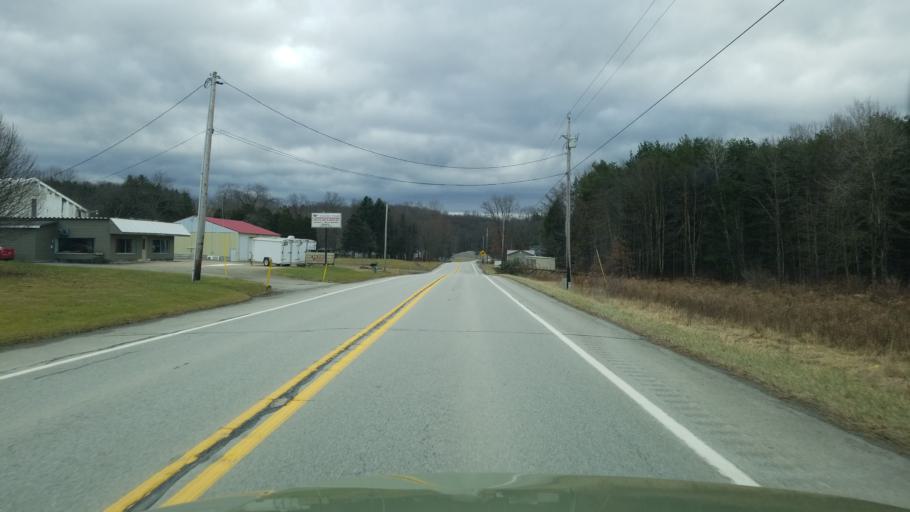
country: US
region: Pennsylvania
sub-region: Indiana County
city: Clymer
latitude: 40.7860
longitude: -79.0538
